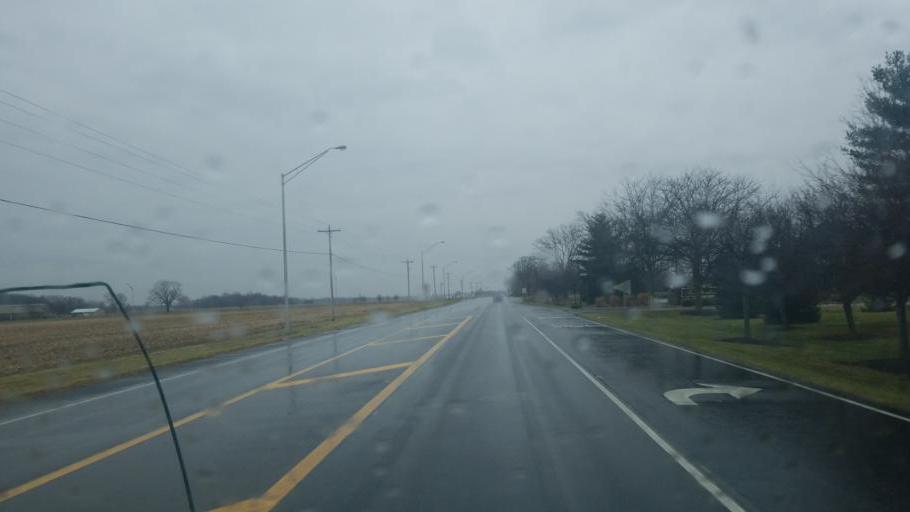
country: US
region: Indiana
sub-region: Shelby County
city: Shelbyville
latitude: 39.4968
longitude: -85.7704
